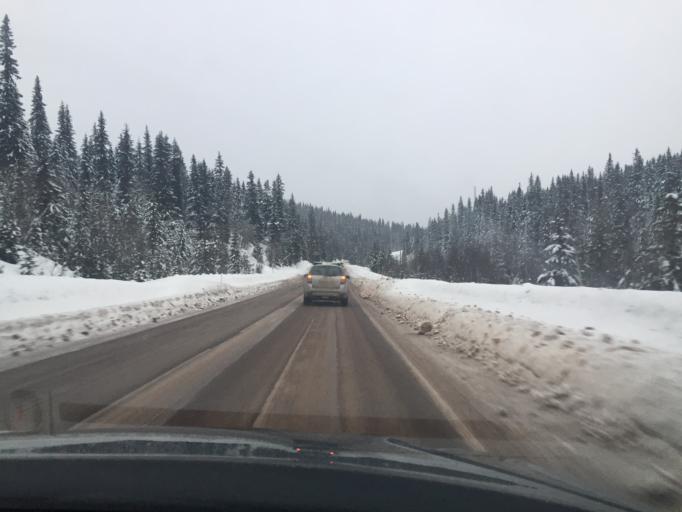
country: SE
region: Dalarna
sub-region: Malung-Saelens kommun
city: Malung
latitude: 61.1622
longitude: 13.1441
